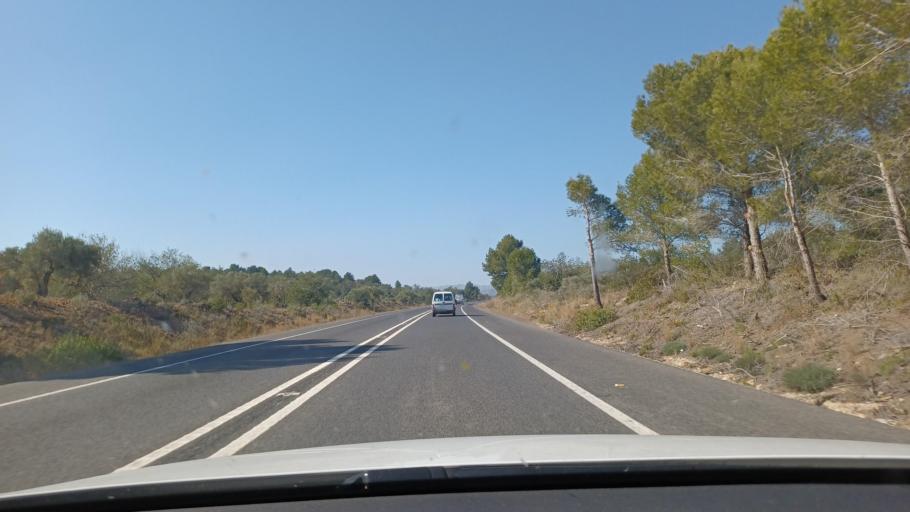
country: ES
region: Catalonia
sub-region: Provincia de Tarragona
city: l'Ametlla de Mar
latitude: 40.8951
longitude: 0.7597
